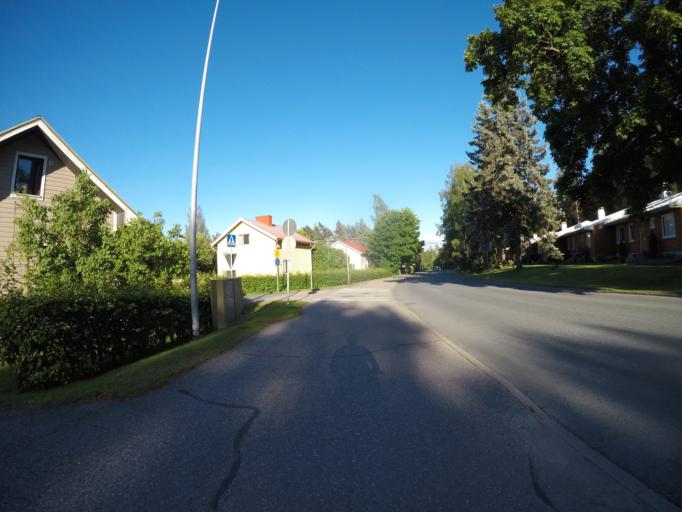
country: FI
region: Haeme
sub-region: Haemeenlinna
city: Haemeenlinna
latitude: 60.9827
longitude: 24.4503
